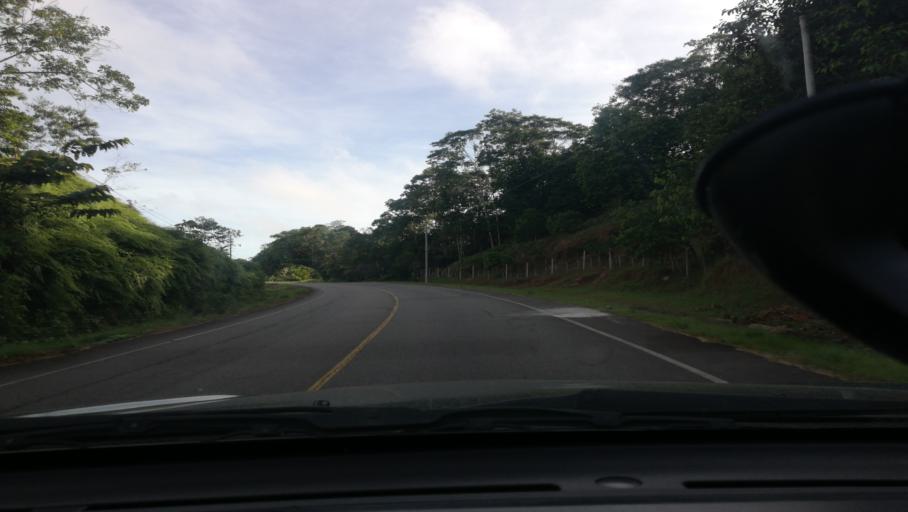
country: PE
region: Loreto
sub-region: Provincia de Loreto
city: Nauta
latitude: -4.4167
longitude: -73.5841
